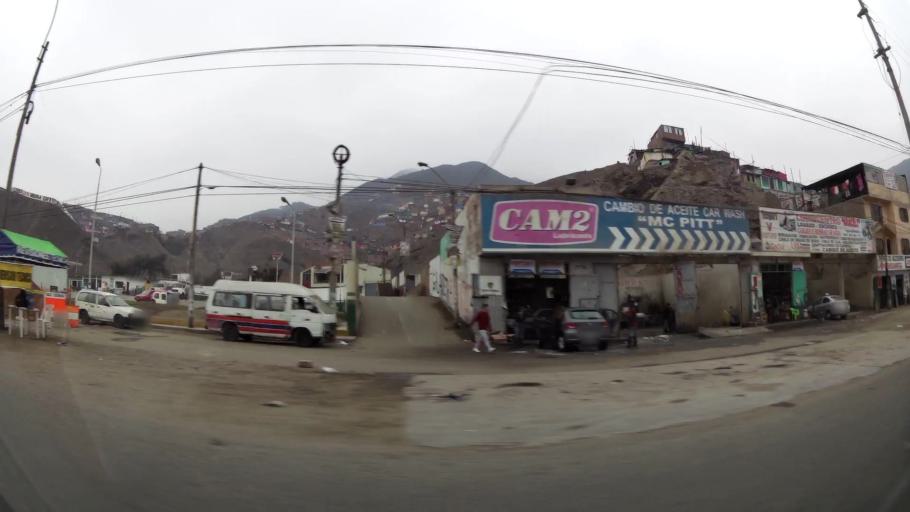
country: PE
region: Lima
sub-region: Lima
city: Urb. Santo Domingo
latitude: -11.9020
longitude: -77.0304
